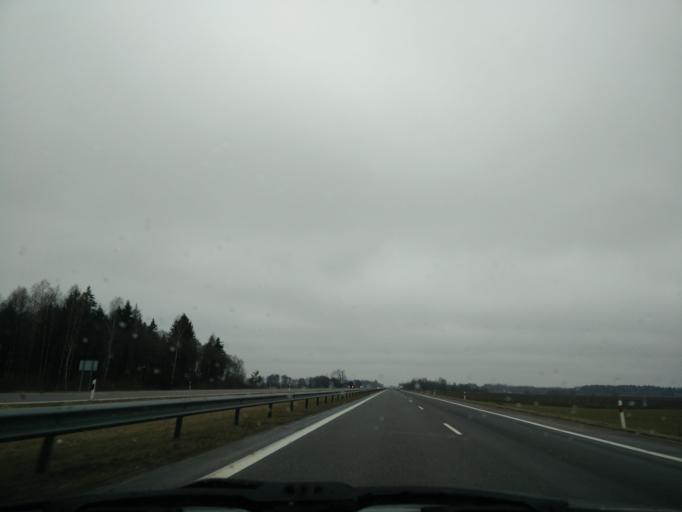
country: LT
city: Raseiniai
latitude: 55.3794
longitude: 22.9277
